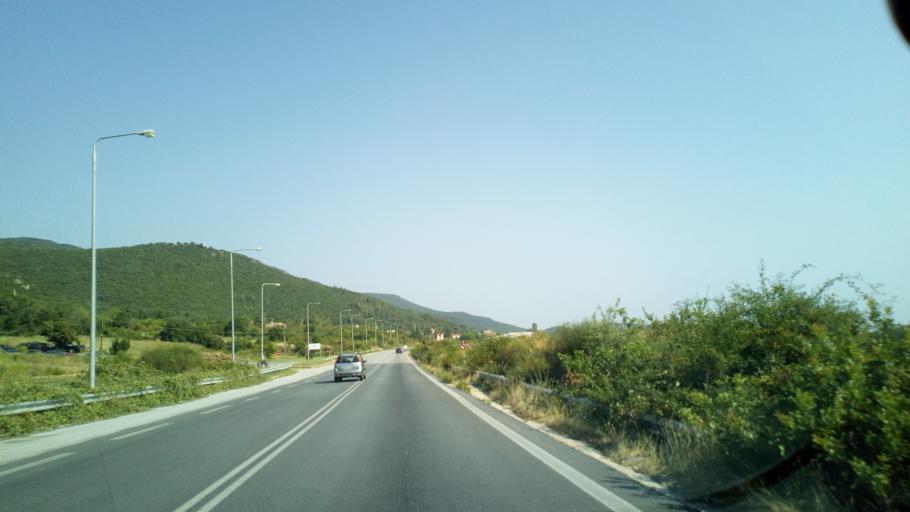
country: GR
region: Central Macedonia
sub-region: Nomos Chalkidikis
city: Polygyros
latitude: 40.3930
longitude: 23.4329
